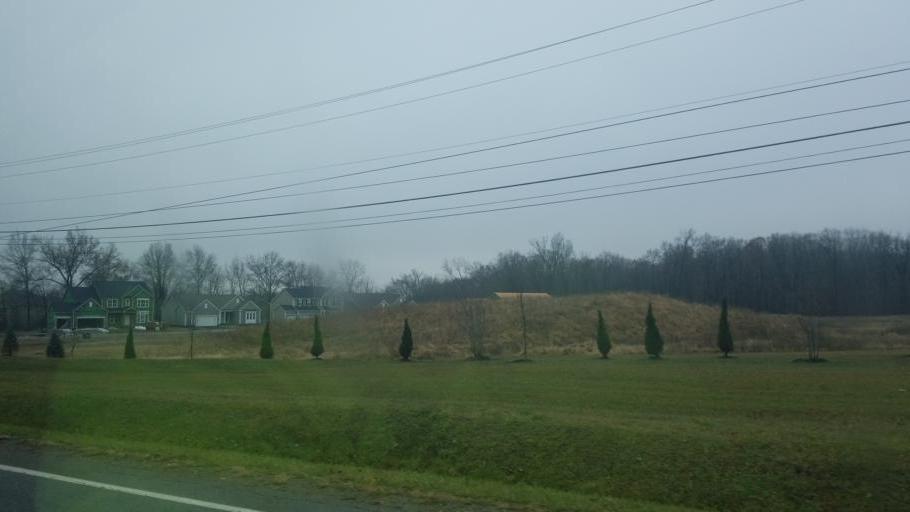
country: US
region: Ohio
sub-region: Union County
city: New California
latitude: 40.1496
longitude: -83.2264
